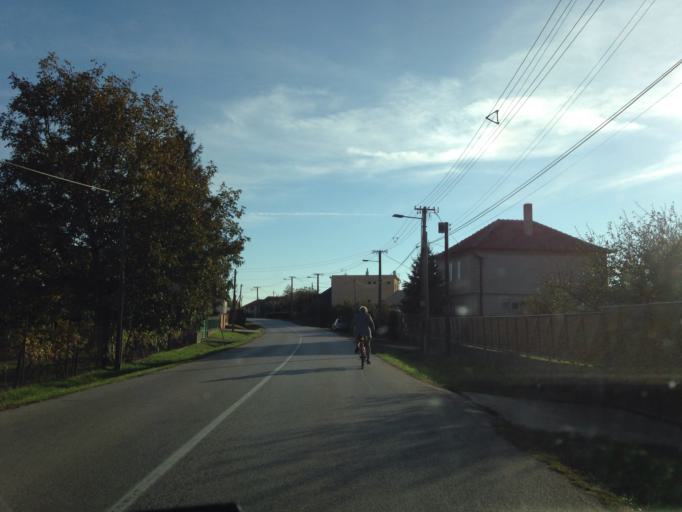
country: SK
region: Nitriansky
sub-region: Okres Komarno
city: Hurbanovo
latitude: 47.9077
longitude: 18.3087
